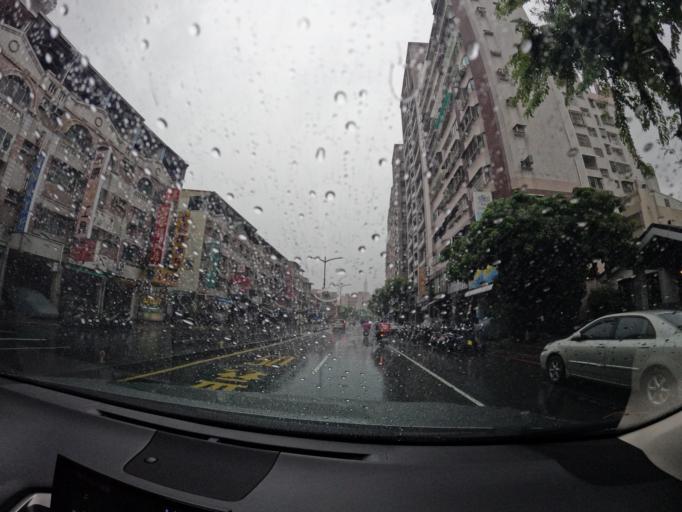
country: TW
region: Kaohsiung
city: Kaohsiung
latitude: 22.6631
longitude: 120.3219
